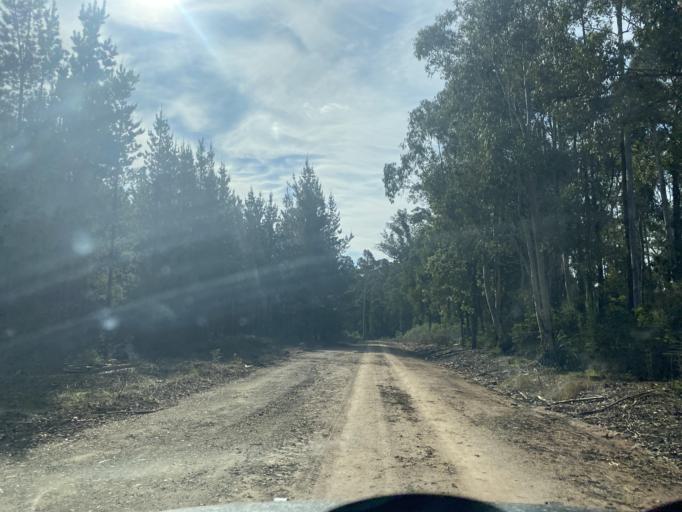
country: AU
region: Victoria
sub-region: Mansfield
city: Mansfield
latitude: -36.8817
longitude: 146.1927
